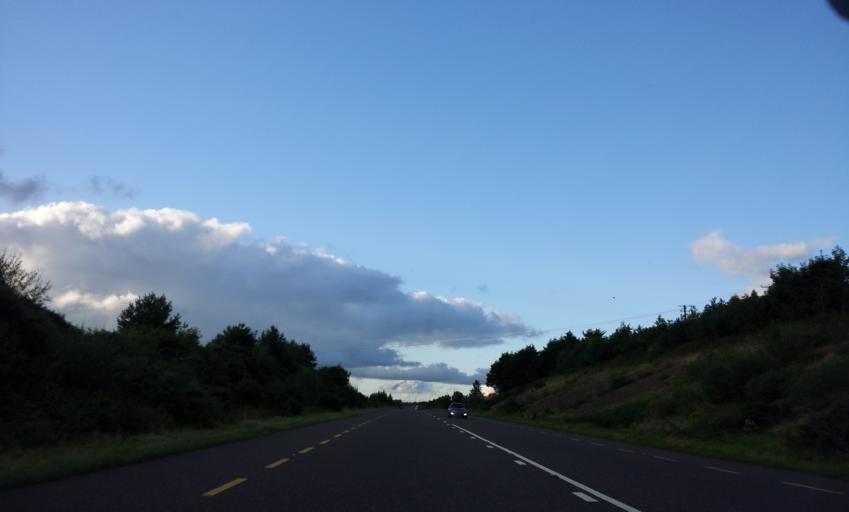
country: IE
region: Munster
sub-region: County Limerick
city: Abbeyfeale
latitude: 52.3203
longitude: -9.3595
